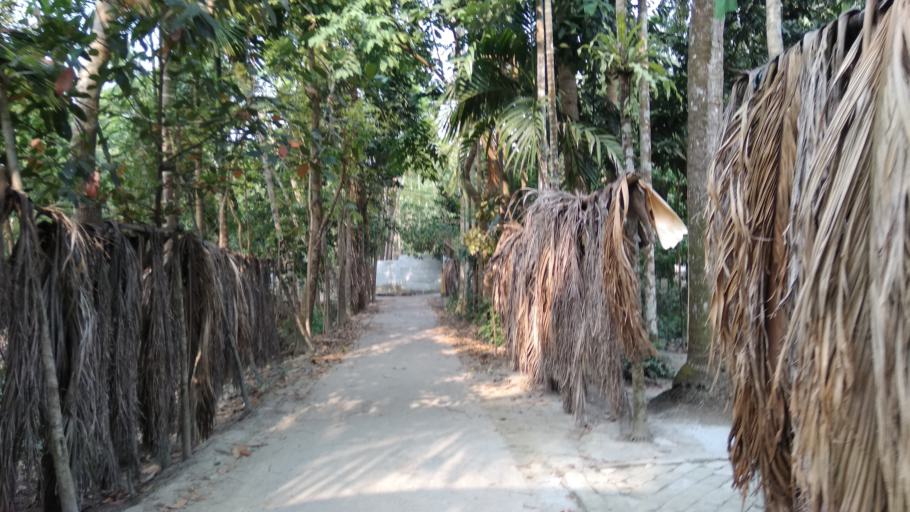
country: BD
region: Barisal
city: Mehendiganj
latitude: 22.9502
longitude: 90.4152
